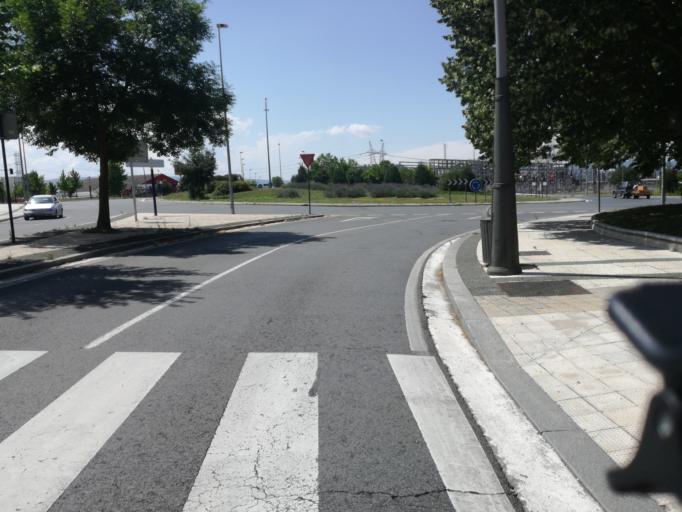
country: ES
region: Basque Country
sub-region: Provincia de Alava
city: Gasteiz / Vitoria
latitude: 42.8551
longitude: -2.7055
